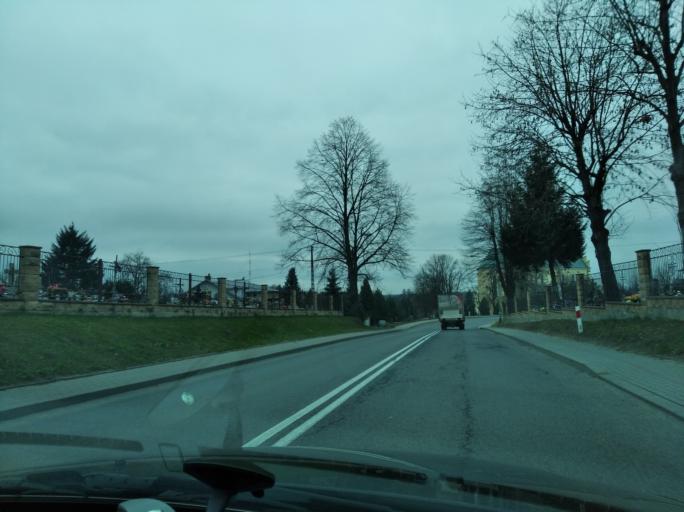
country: PL
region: Subcarpathian Voivodeship
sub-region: Powiat lancucki
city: Zolynia
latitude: 50.1689
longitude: 22.3104
